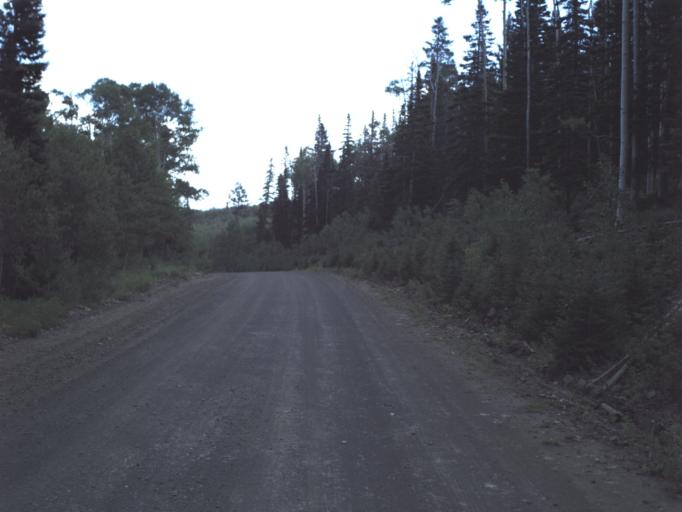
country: US
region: Utah
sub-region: Piute County
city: Junction
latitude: 38.2454
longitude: -112.3433
